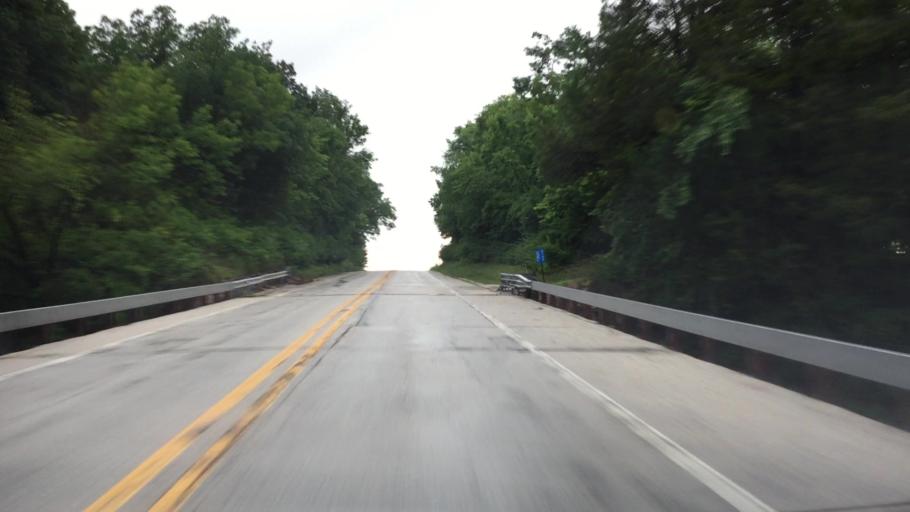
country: US
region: Illinois
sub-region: Hancock County
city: Nauvoo
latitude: 40.5164
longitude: -91.3590
